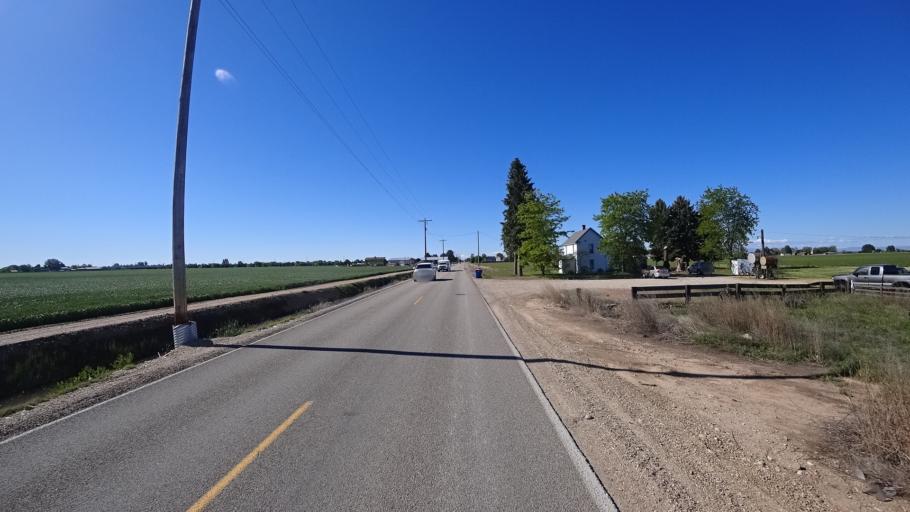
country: US
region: Idaho
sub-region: Ada County
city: Star
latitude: 43.6417
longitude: -116.4536
